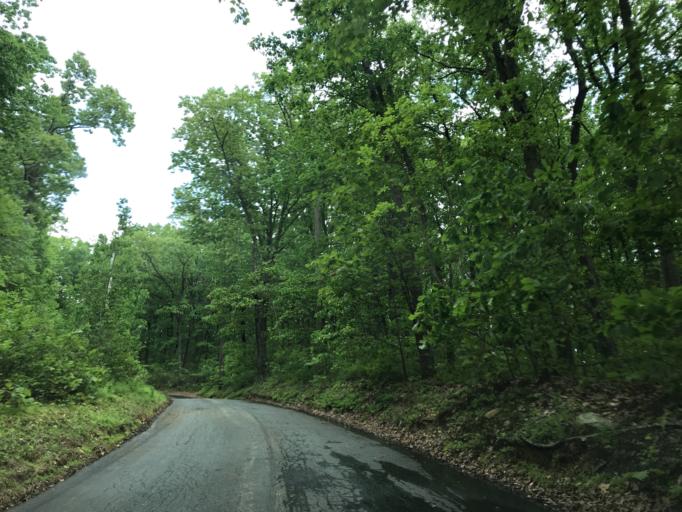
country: US
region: Pennsylvania
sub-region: York County
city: Susquehanna Trails
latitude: 39.6934
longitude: -76.3648
